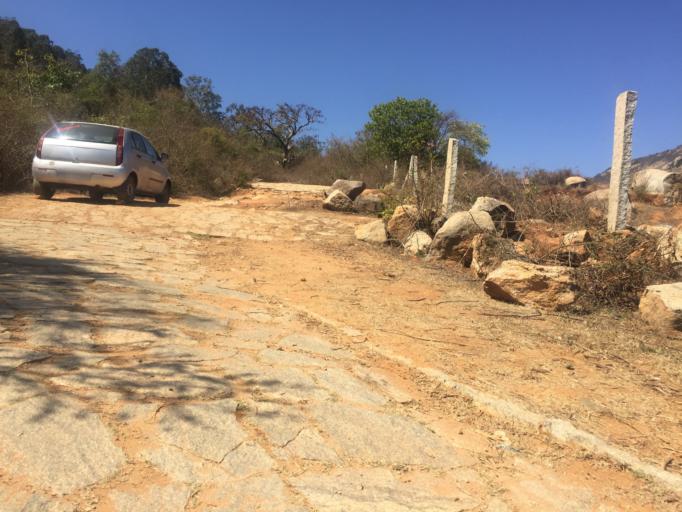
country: IN
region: Karnataka
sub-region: Chikkaballapur
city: Chik Ballapur
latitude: 13.3787
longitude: 77.6808
